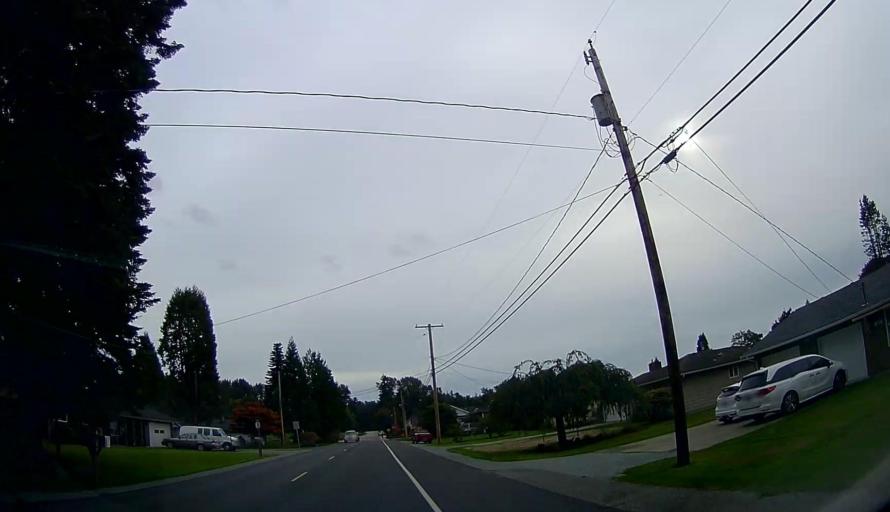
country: US
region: Washington
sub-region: Skagit County
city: Burlington
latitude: 48.4725
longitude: -122.3084
